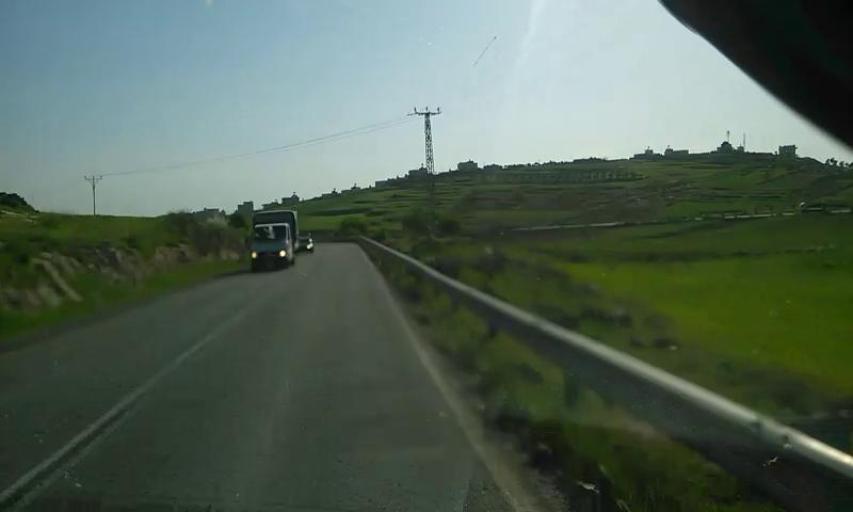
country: PS
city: Al Hilah
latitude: 31.4732
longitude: 35.1324
